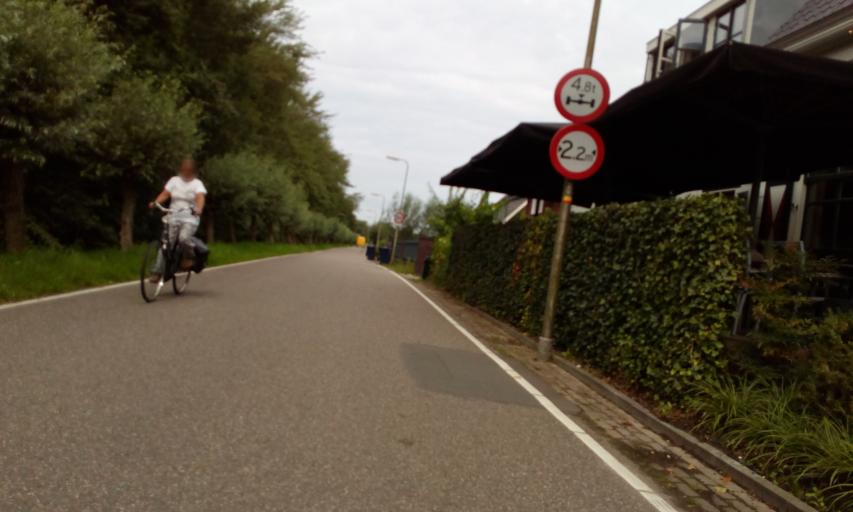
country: NL
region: South Holland
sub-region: Gemeente Krimpen aan den IJssel
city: Krimpen aan den IJssel
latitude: 51.9453
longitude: 4.6023
